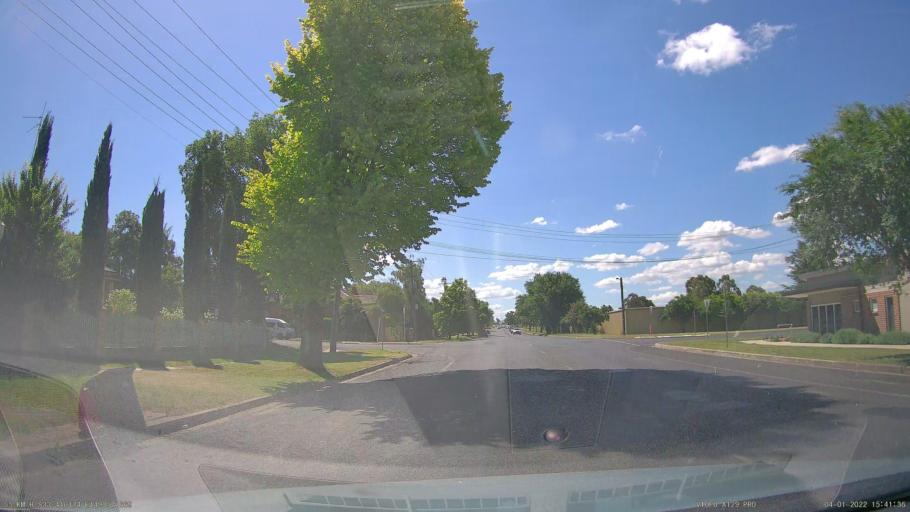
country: AU
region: New South Wales
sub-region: Bathurst Regional
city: Bathurst
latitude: -33.4099
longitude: 149.5775
